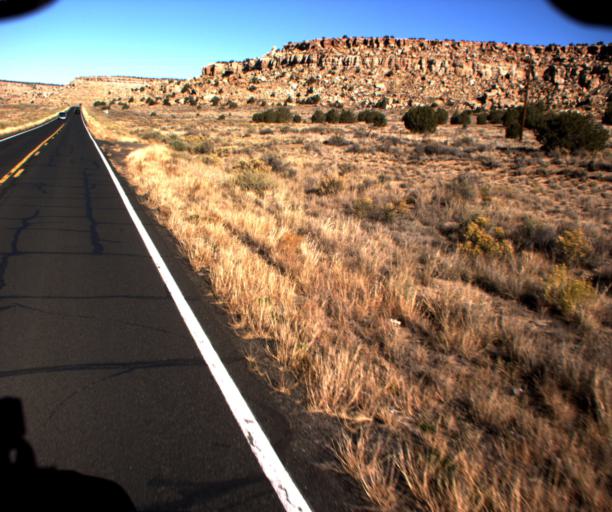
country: US
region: Arizona
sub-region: Navajo County
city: First Mesa
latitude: 35.8289
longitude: -110.2234
